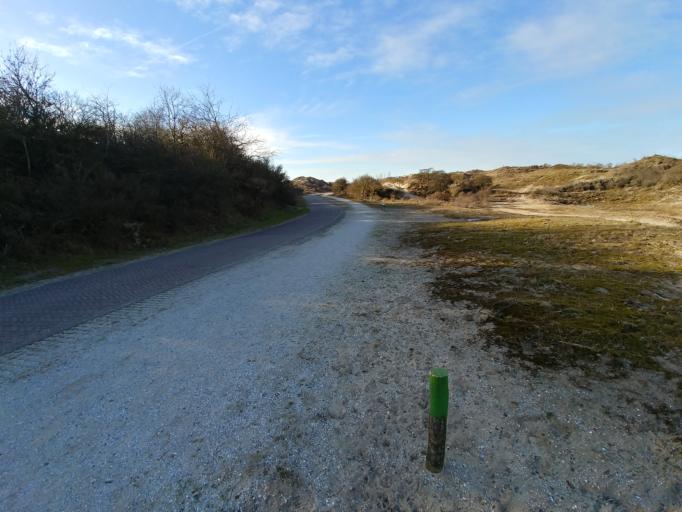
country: NL
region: South Holland
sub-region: Gemeente Den Haag
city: Scheveningen
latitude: 52.1353
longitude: 4.3258
